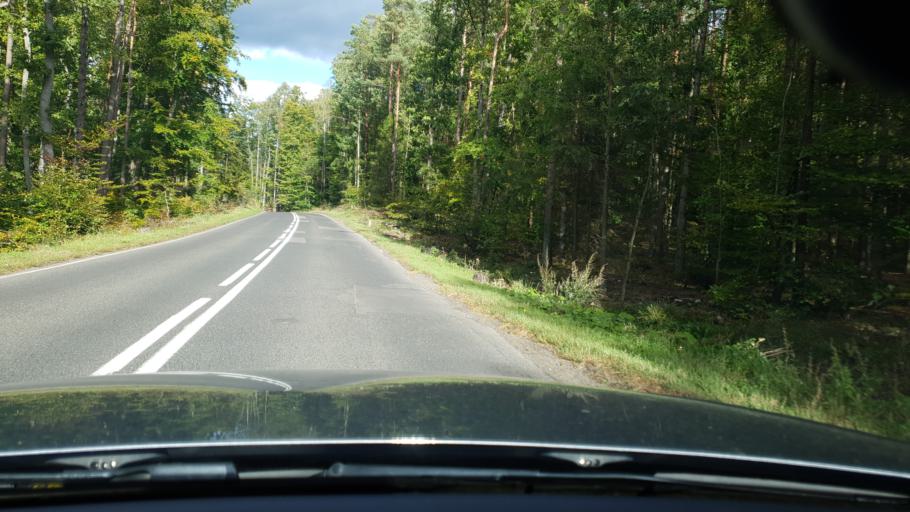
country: PL
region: Pomeranian Voivodeship
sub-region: Powiat wejherowski
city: Koleczkowo
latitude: 54.5042
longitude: 18.3686
